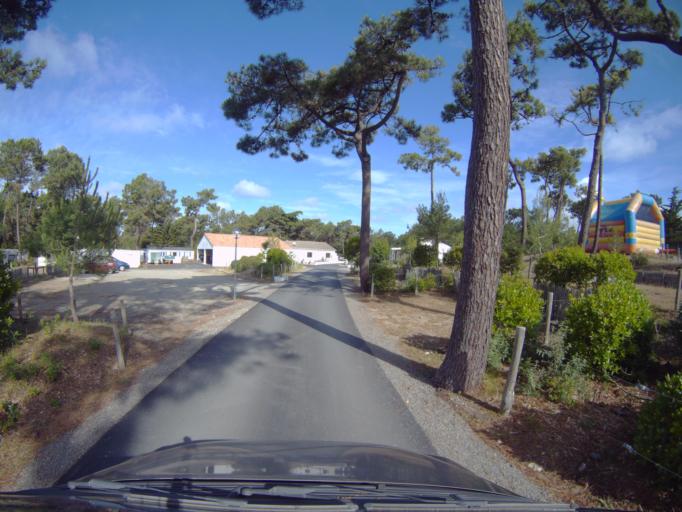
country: FR
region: Pays de la Loire
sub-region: Departement de la Vendee
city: La Barre-de-Monts
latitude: 46.8834
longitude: -2.1485
